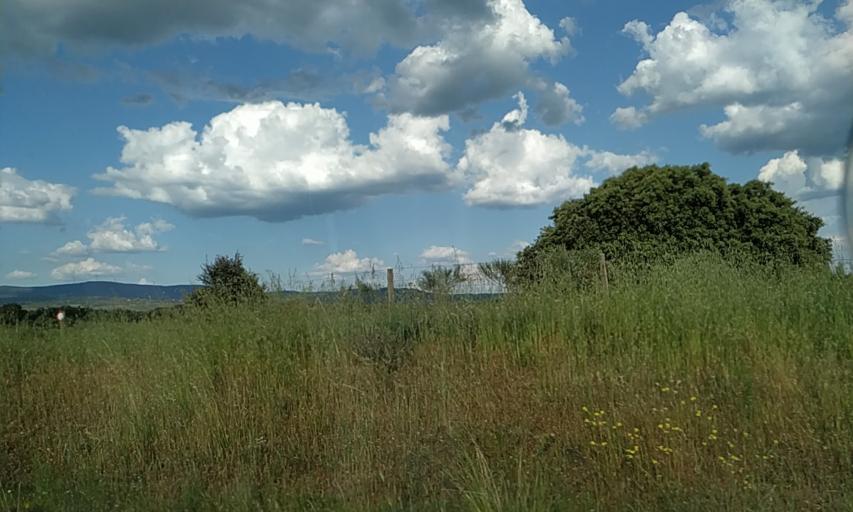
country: PT
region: Portalegre
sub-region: Portalegre
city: Portalegre
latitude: 39.2517
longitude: -7.4481
